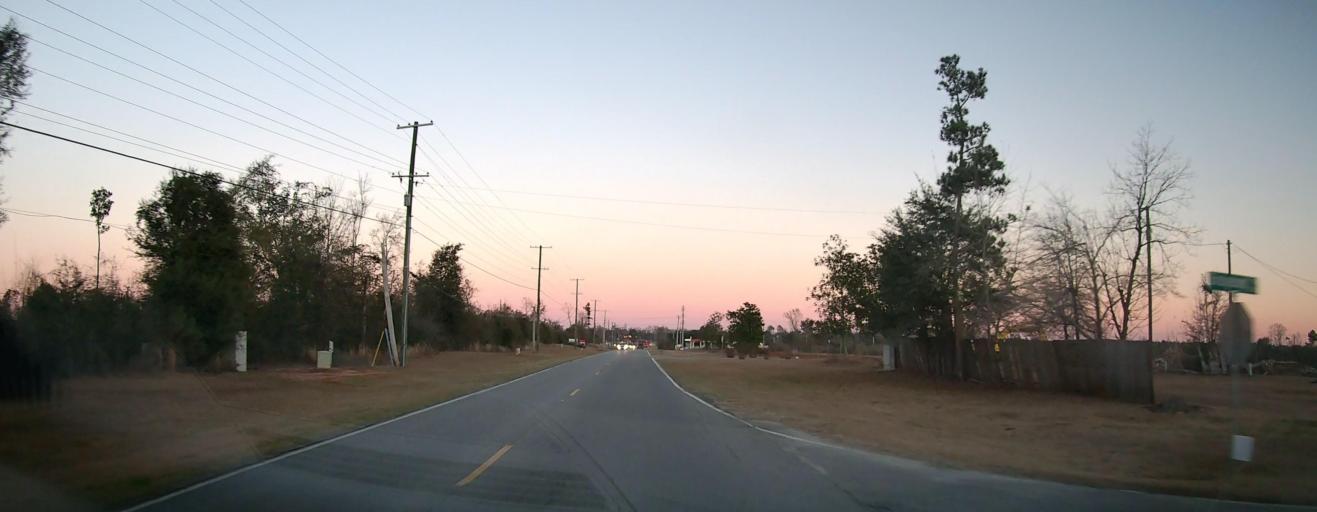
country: US
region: Georgia
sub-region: Dougherty County
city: Putney
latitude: 31.5292
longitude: -84.1208
